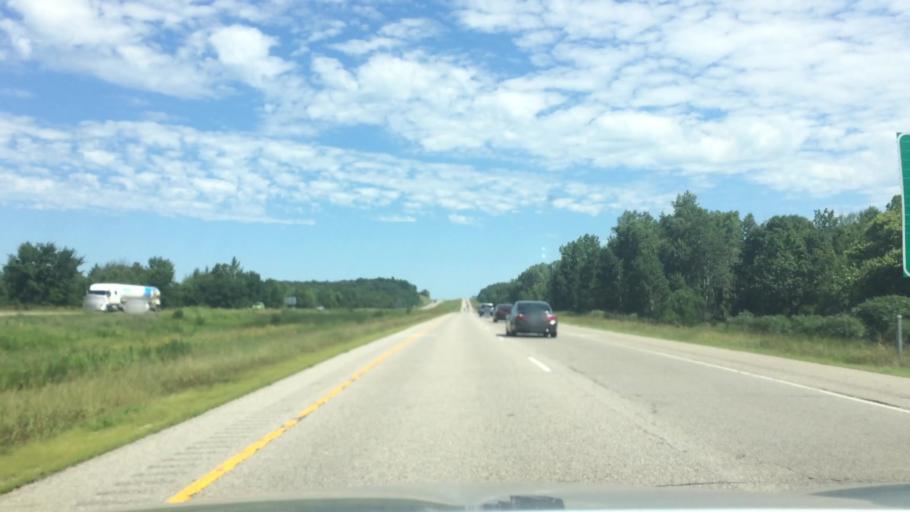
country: US
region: Wisconsin
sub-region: Marquette County
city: Westfield
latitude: 43.7703
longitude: -89.4845
